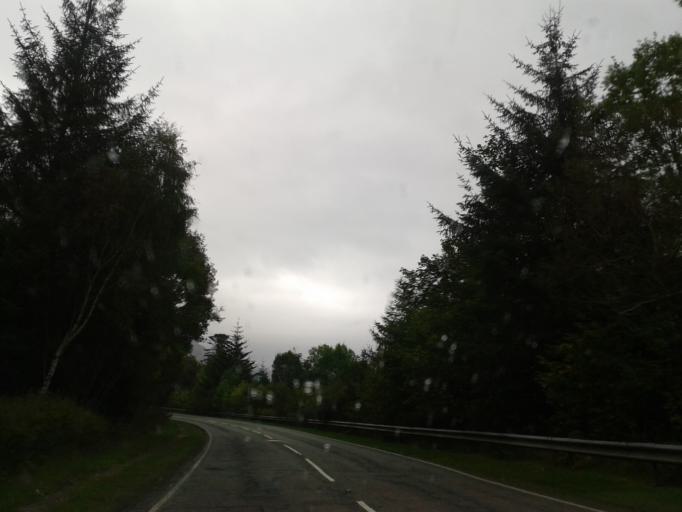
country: GB
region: Scotland
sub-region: Highland
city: Fort William
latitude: 57.2406
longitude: -5.4552
